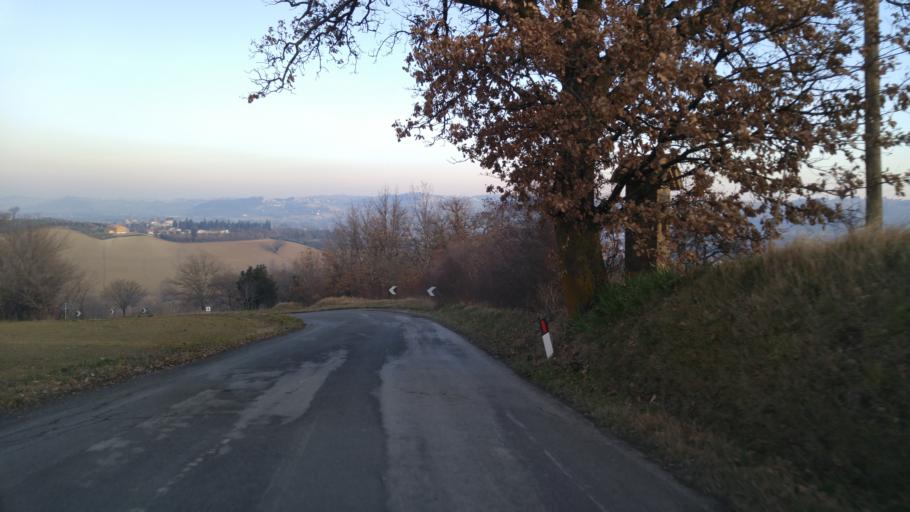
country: IT
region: The Marches
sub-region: Provincia di Pesaro e Urbino
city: Monte Porzio
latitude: 43.6942
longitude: 13.0356
